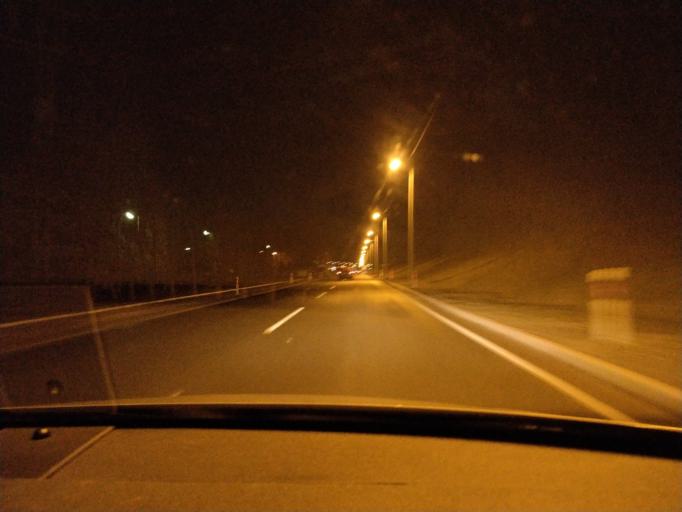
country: HR
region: Grad Zagreb
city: Novi Zagreb
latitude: 45.7793
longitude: 15.9486
